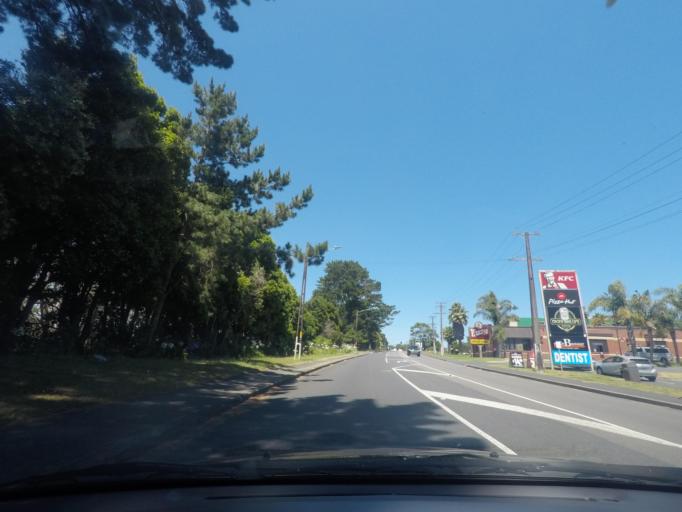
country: NZ
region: Auckland
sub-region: Auckland
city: Waitakere
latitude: -36.9242
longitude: 174.7226
